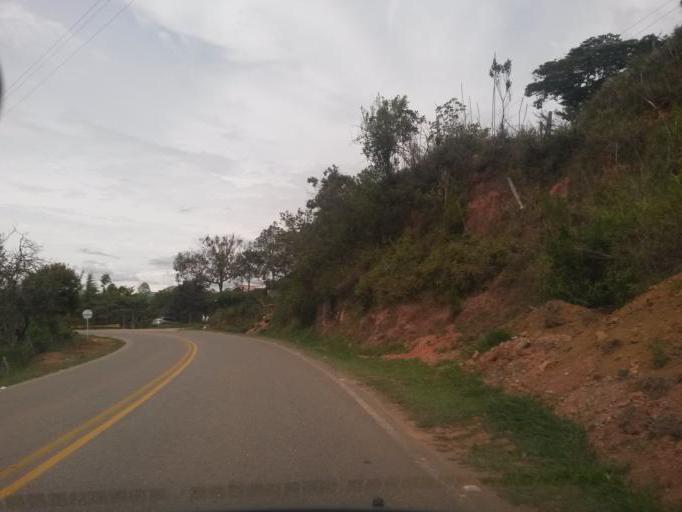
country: CO
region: Cauca
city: Lopez
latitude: 2.4335
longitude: -76.7692
